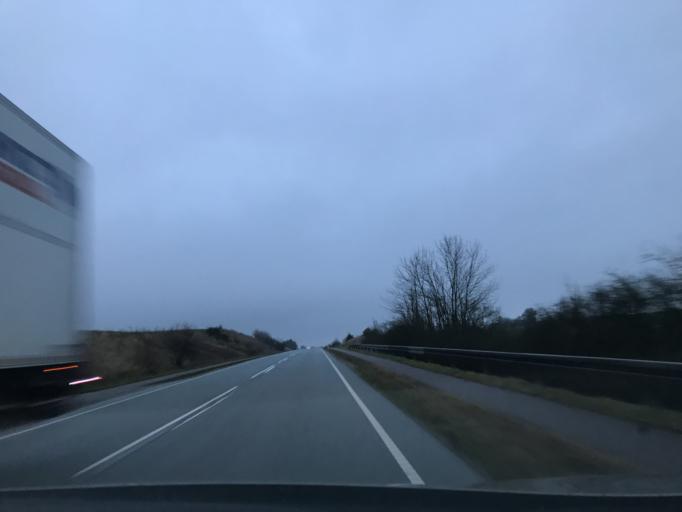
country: DK
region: Central Jutland
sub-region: Hedensted Kommune
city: Hedensted
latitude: 55.7066
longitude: 9.7524
